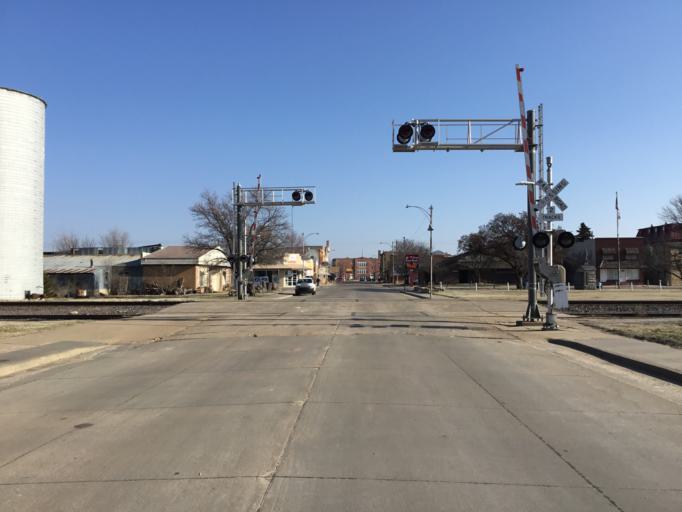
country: US
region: Kansas
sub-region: Ellsworth County
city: Ellsworth
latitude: 38.8247
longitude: -98.4741
